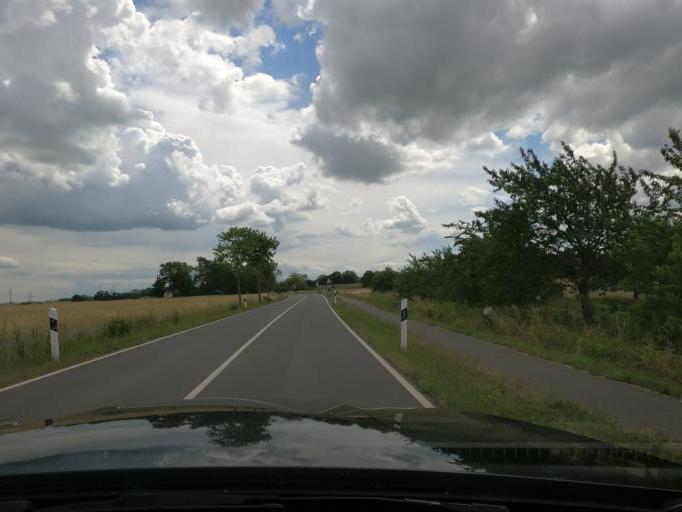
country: DE
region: Lower Saxony
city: Sehnde
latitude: 52.3043
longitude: 9.9788
